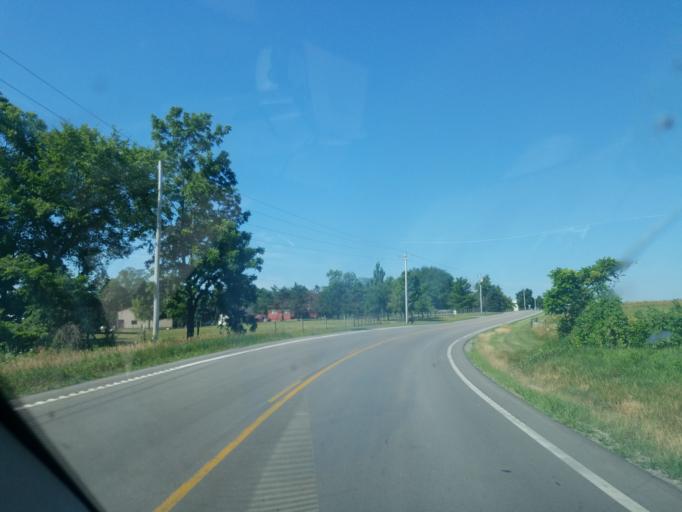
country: US
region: Ohio
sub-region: Logan County
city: Northwood
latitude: 40.4468
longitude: -83.7701
